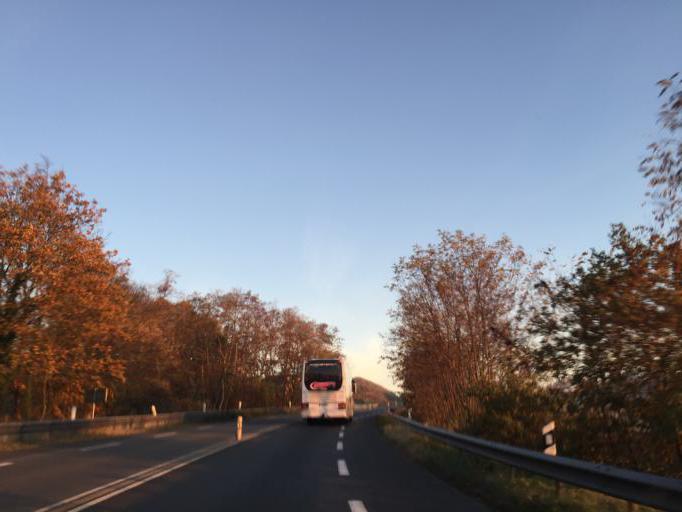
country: FR
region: Rhone-Alpes
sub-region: Departement de la Loire
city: Neulise
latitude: 45.8702
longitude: 4.1741
